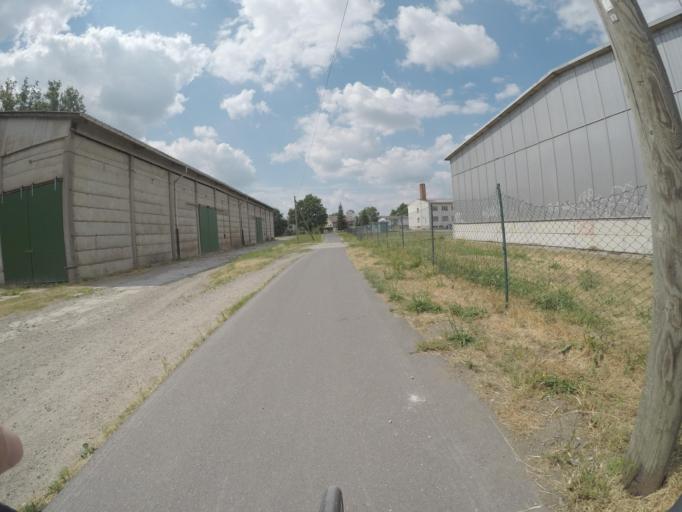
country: DE
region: Brandenburg
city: Roskow
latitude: 52.4609
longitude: 12.6814
